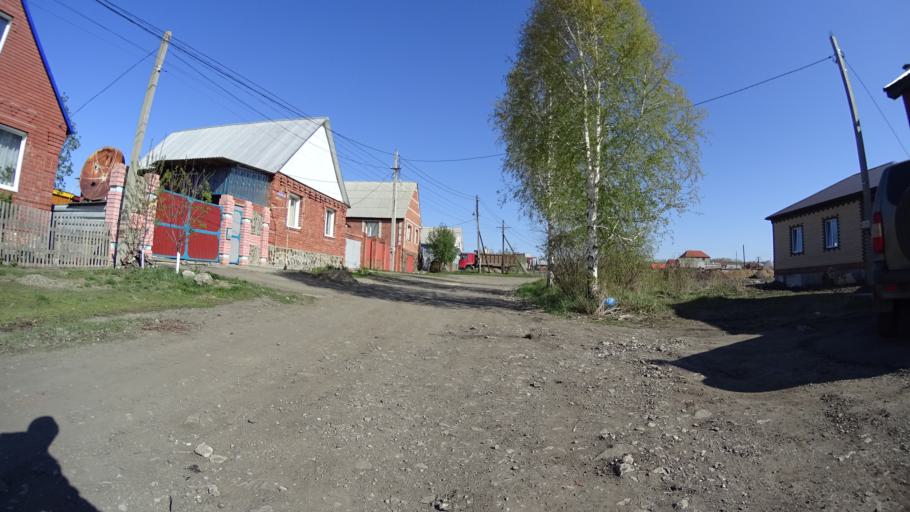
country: RU
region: Chelyabinsk
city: Troitsk
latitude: 54.0950
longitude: 61.5968
